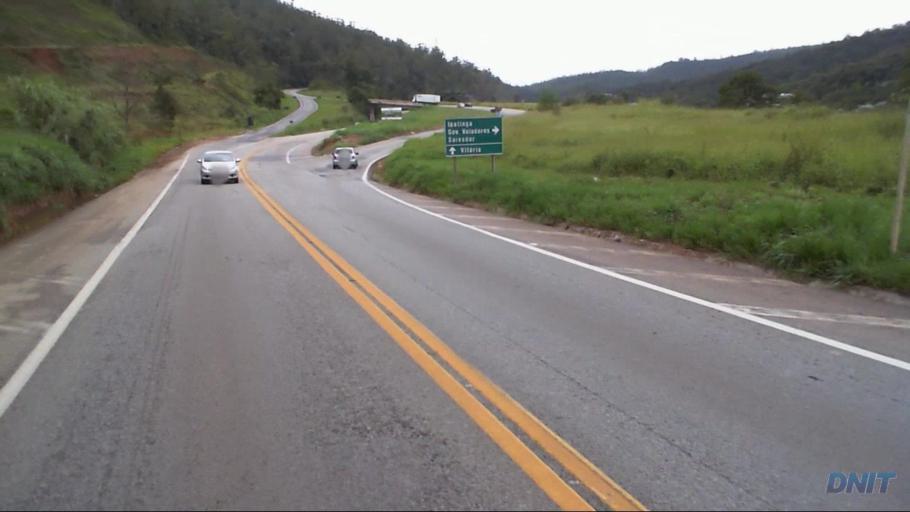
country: BR
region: Minas Gerais
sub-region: Joao Monlevade
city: Joao Monlevade
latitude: -19.8614
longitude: -43.1186
